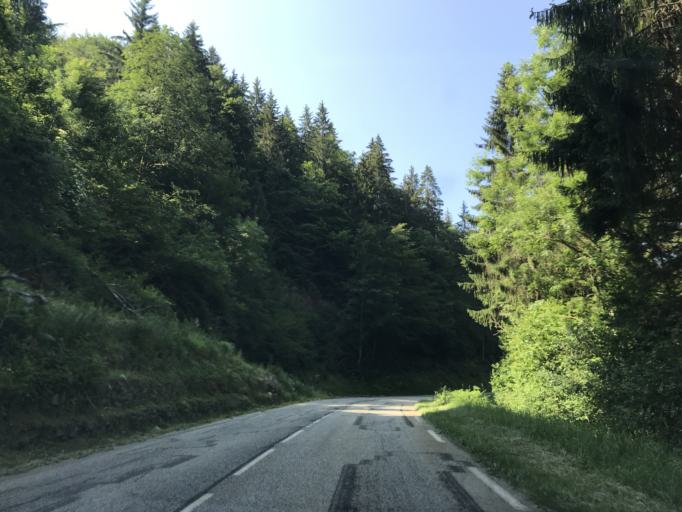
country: FR
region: Rhone-Alpes
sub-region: Departement de l'Isere
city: Allevard
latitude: 45.3371
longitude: 6.0935
